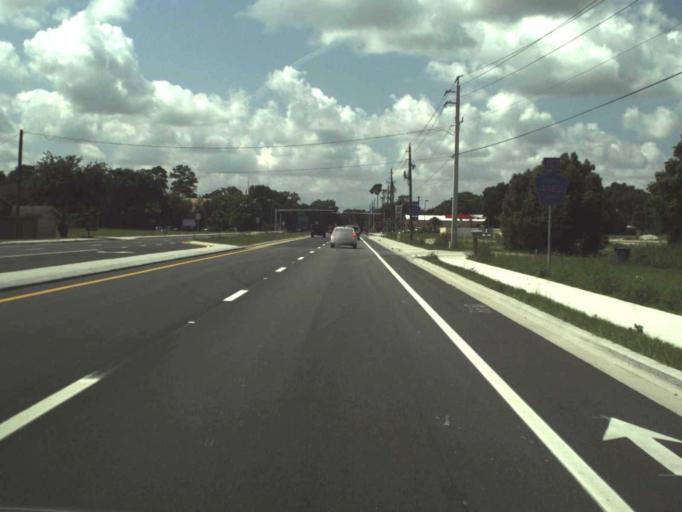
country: US
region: Florida
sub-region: Seminole County
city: Midway
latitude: 28.8532
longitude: -81.1622
